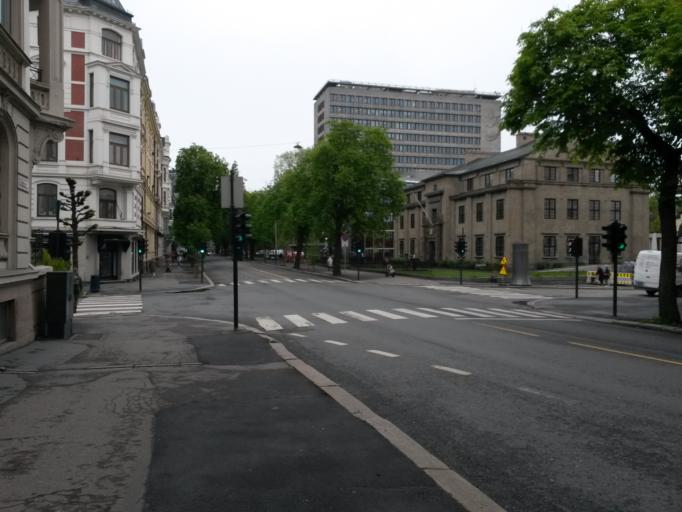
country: NO
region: Oslo
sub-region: Oslo
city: Sjolyststranda
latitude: 59.9157
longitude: 10.7129
